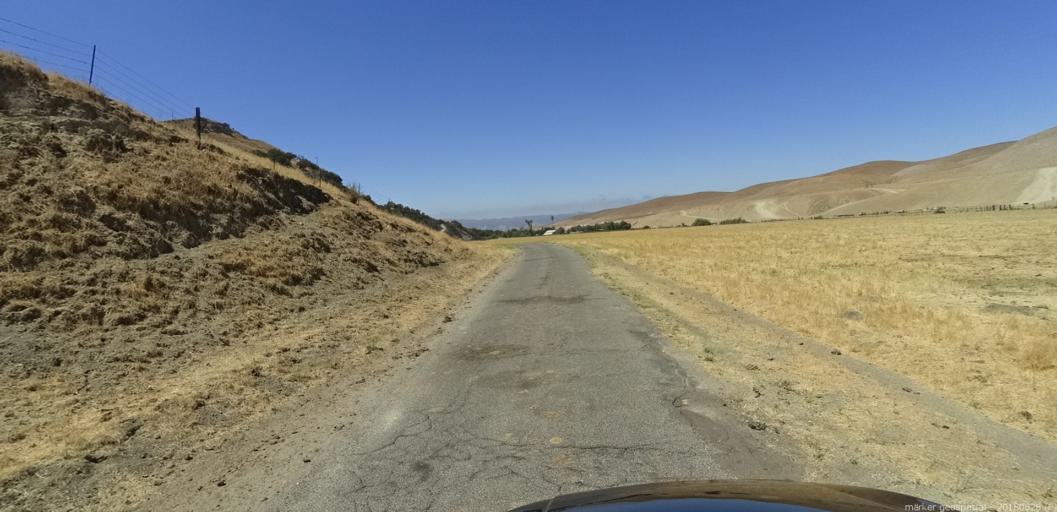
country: US
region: California
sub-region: San Luis Obispo County
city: San Miguel
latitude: 36.0494
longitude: -120.8154
